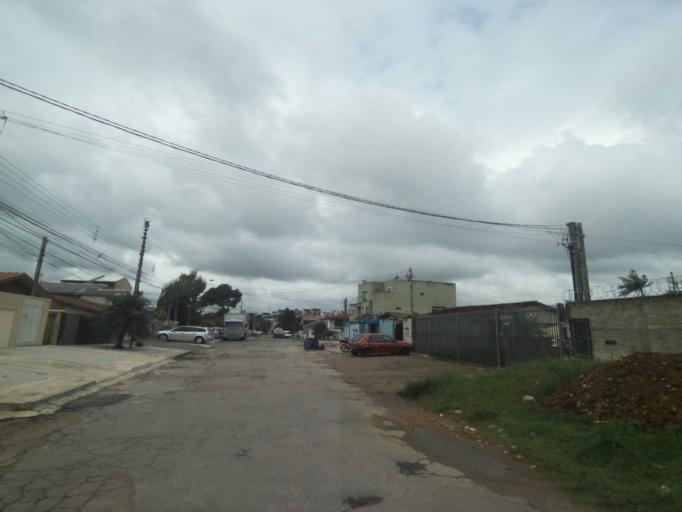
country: BR
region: Parana
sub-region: Curitiba
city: Curitiba
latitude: -25.4863
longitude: -49.3122
